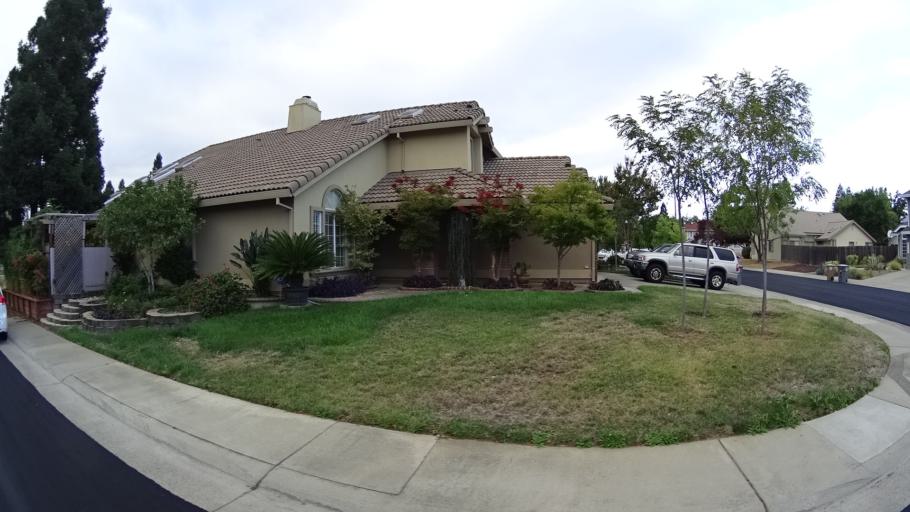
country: US
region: California
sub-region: Sacramento County
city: Laguna
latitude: 38.4284
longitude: -121.4372
